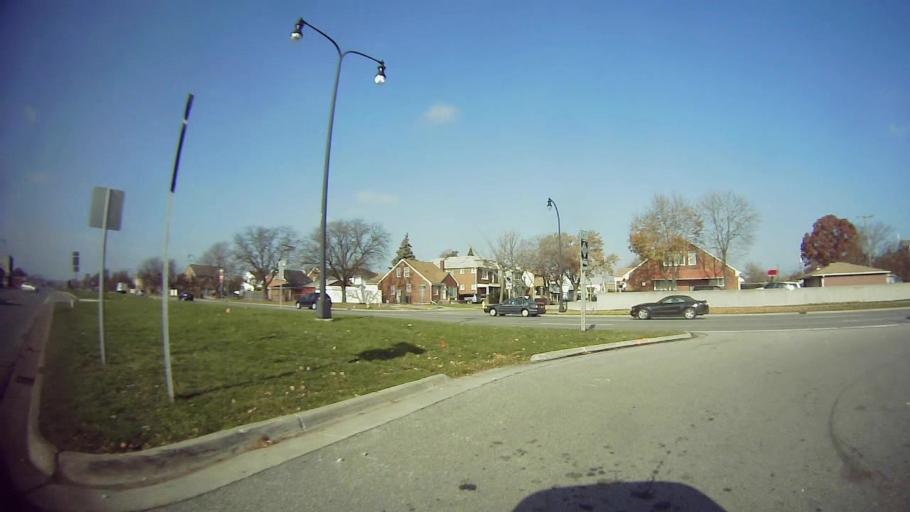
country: US
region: Michigan
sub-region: Wayne County
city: Dearborn
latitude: 42.3297
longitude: -83.1801
